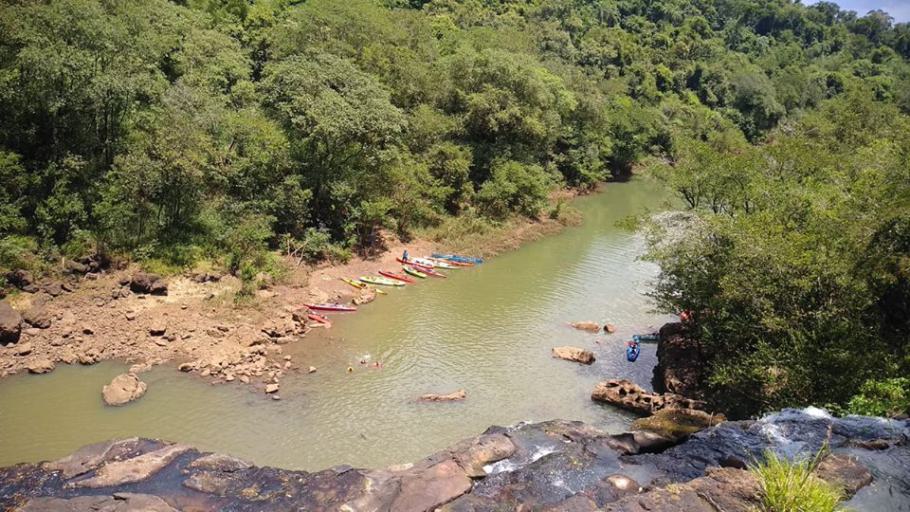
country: AR
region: Misiones
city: Puerto Libertad
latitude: -25.8288
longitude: -54.5800
